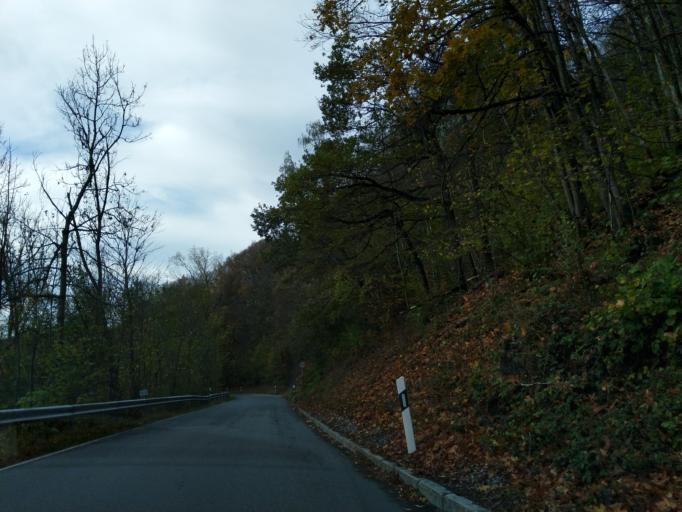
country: DE
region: Bavaria
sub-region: Lower Bavaria
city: Schofweg
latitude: 48.8103
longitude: 13.2324
